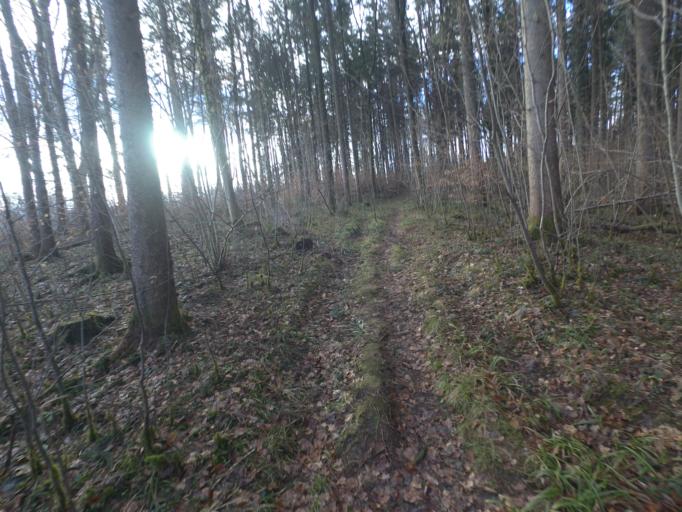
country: AT
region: Salzburg
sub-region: Politischer Bezirk Salzburg-Umgebung
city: Anif
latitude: 47.7683
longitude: 13.0571
